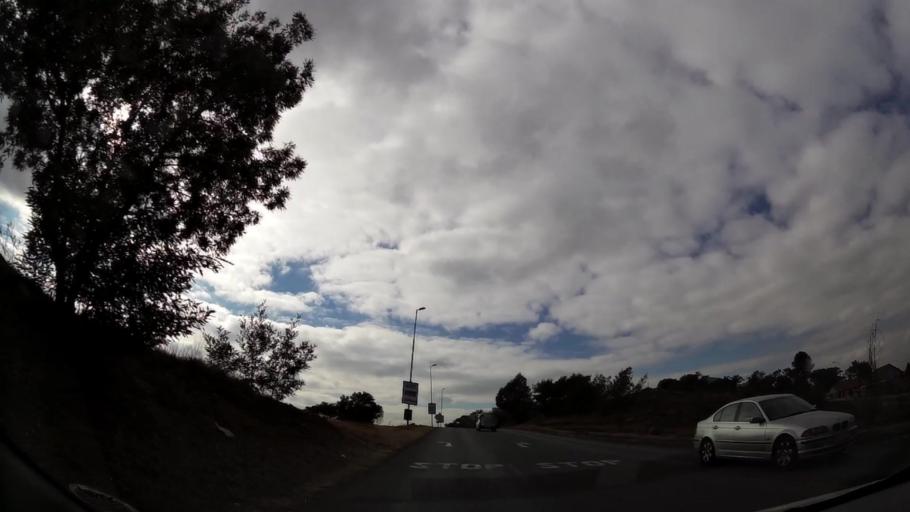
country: ZA
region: Gauteng
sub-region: City of Johannesburg Metropolitan Municipality
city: Roodepoort
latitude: -26.1073
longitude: 27.8654
